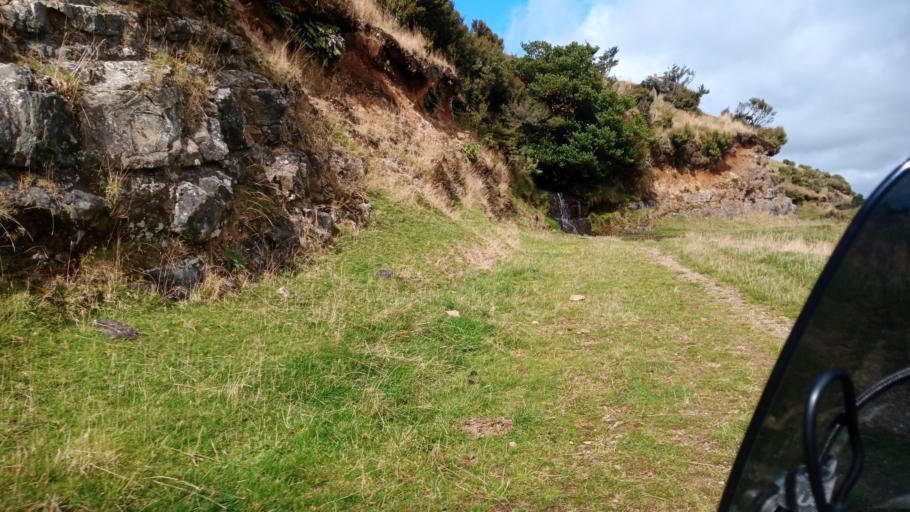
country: NZ
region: Gisborne
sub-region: Gisborne District
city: Gisborne
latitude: -38.4724
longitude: 177.5359
